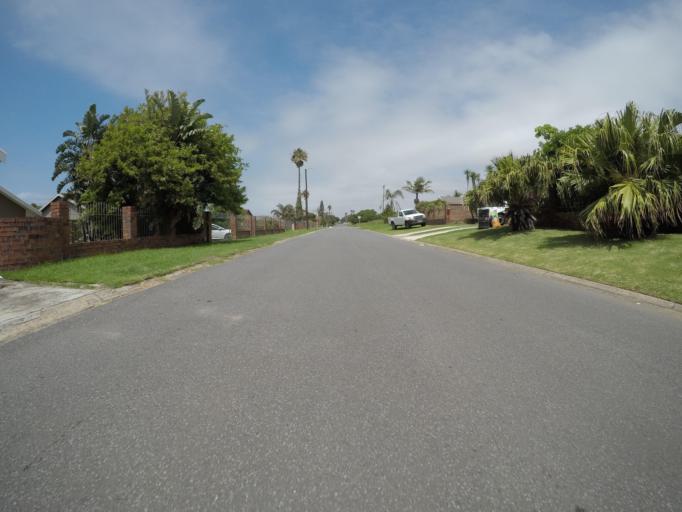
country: ZA
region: Eastern Cape
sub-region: Buffalo City Metropolitan Municipality
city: East London
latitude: -32.9467
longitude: 28.0181
